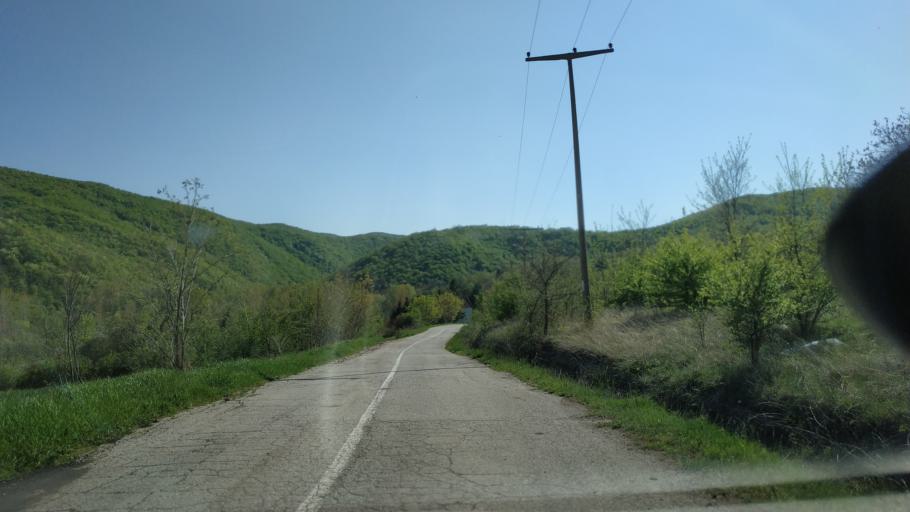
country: RS
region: Central Serbia
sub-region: Nisavski Okrug
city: Nis
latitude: 43.4288
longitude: 21.8511
